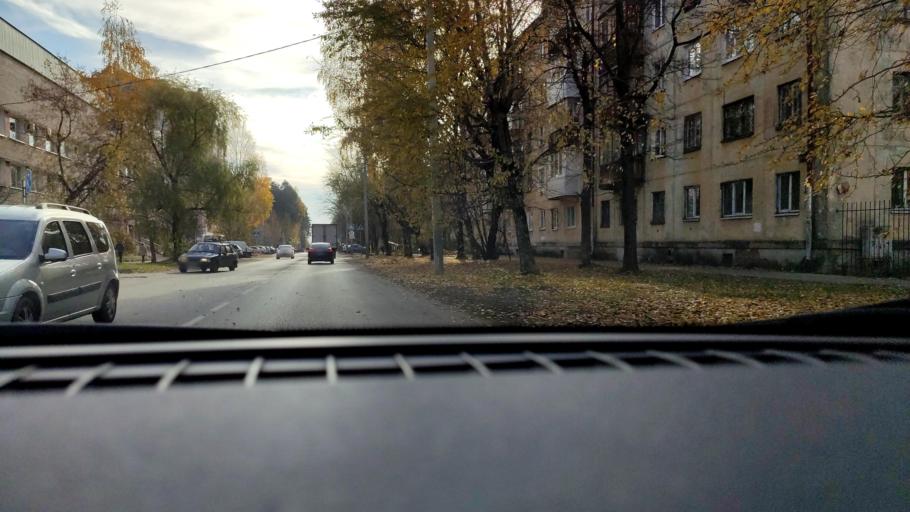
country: RU
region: Perm
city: Kultayevo
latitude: 58.0176
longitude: 55.9783
